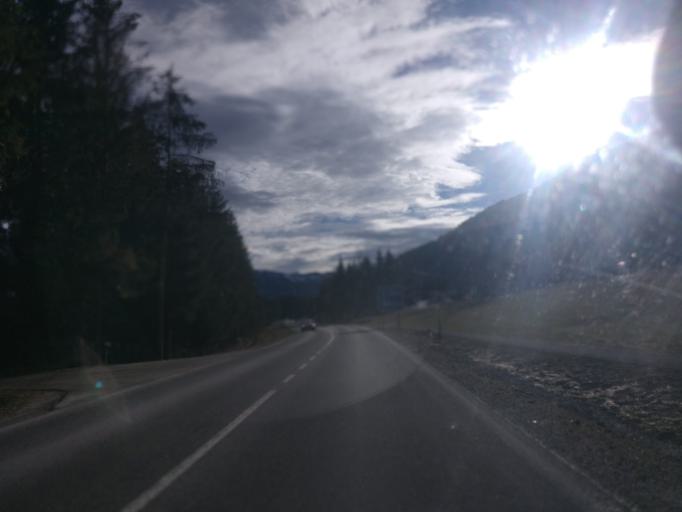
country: AT
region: Styria
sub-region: Politischer Bezirk Liezen
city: Ardning
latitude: 47.5780
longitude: 14.3215
